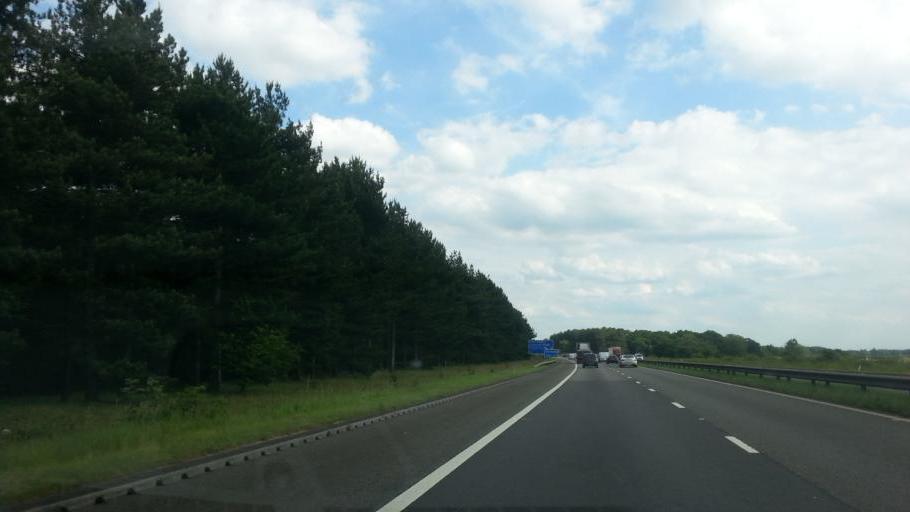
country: GB
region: England
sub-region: Nottinghamshire
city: Bircotes
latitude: 53.4005
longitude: -1.0784
